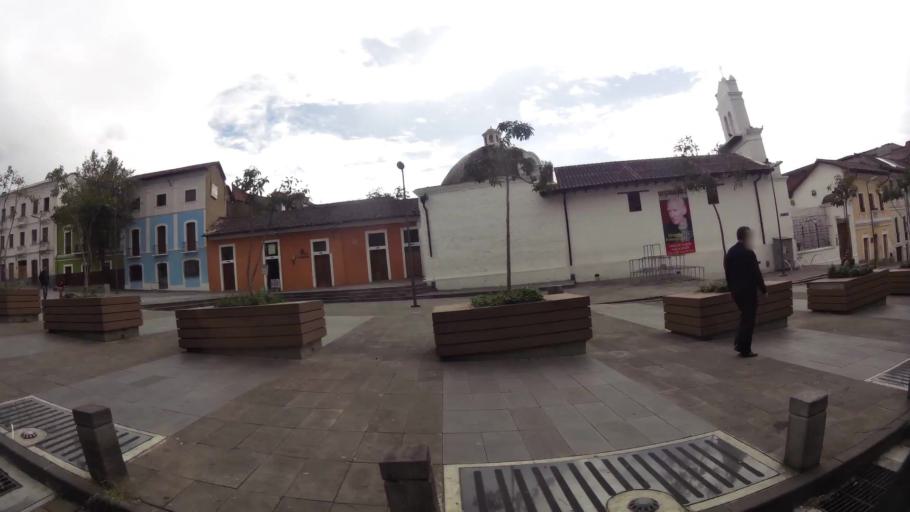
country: EC
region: Pichincha
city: Quito
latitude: -0.2222
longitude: -78.5178
